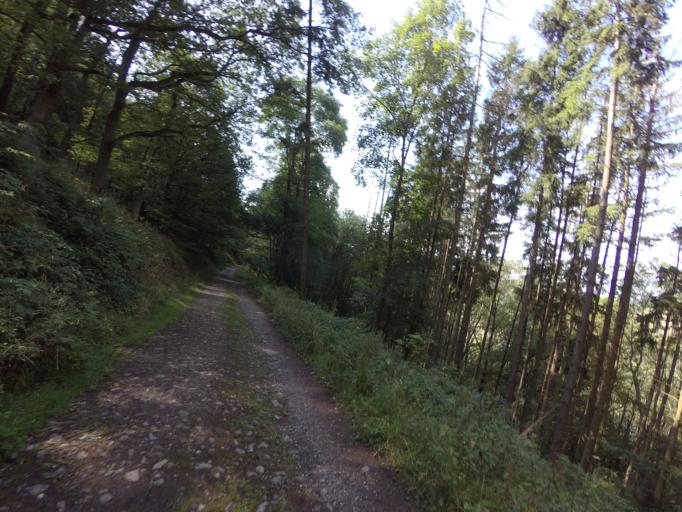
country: DE
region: North Rhine-Westphalia
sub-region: Regierungsbezirk Koln
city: Simmerath
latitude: 50.5929
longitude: 6.3880
